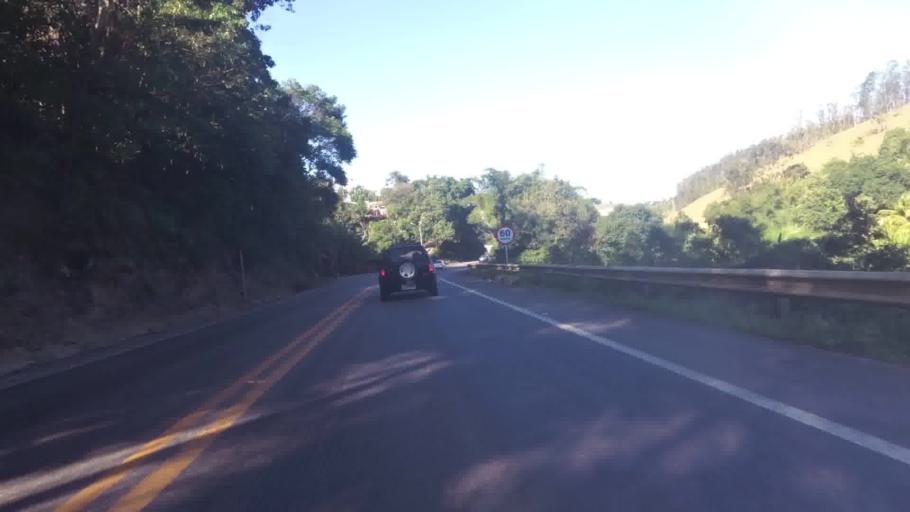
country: BR
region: Espirito Santo
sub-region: Iconha
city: Iconha
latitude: -20.7961
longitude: -40.8184
